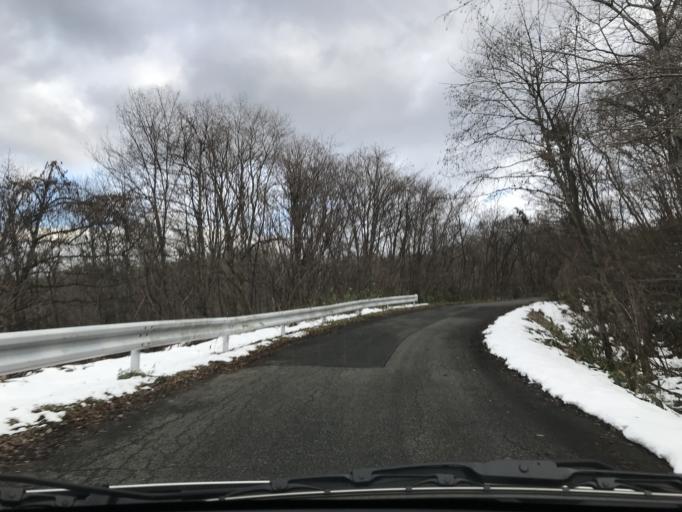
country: JP
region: Iwate
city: Ichinoseki
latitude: 38.9934
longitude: 141.0002
